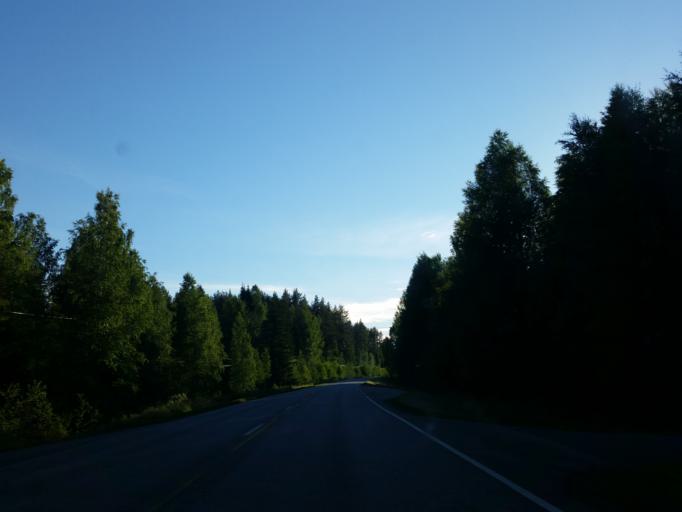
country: FI
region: Northern Savo
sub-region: Kuopio
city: Karttula
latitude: 62.8577
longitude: 27.2175
